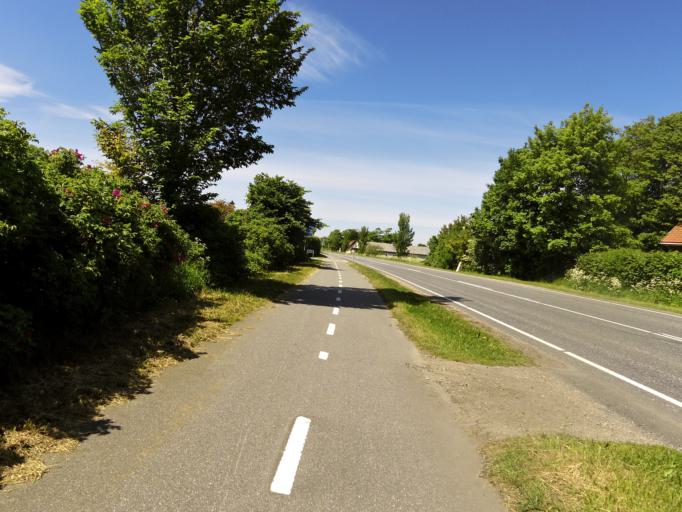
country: DK
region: South Denmark
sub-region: Haderslev Kommune
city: Gram
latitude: 55.2752
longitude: 9.0710
